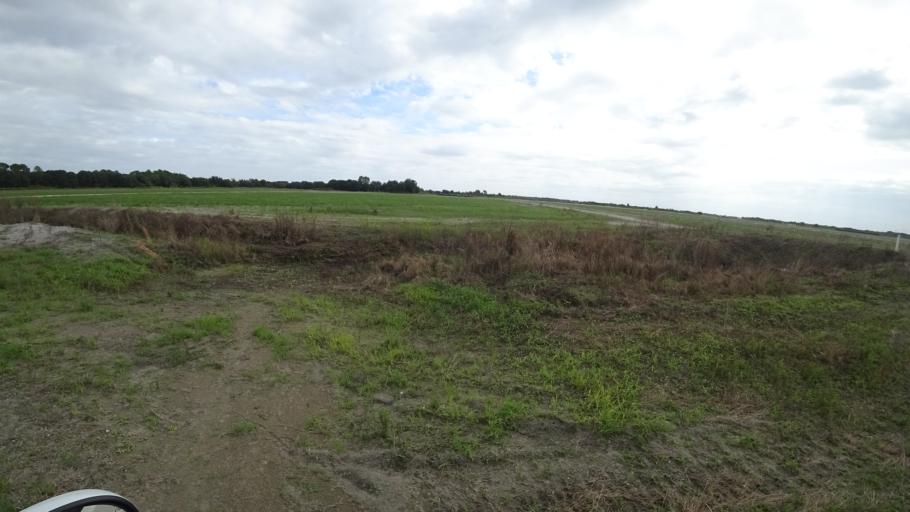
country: US
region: Florida
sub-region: Hillsborough County
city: Wimauma
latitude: 27.5678
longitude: -82.3058
